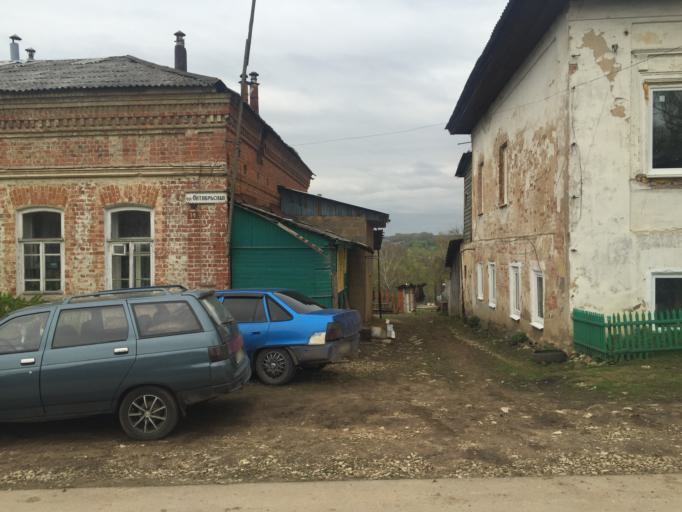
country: RU
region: Tula
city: Krapivna
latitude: 53.9418
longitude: 37.1595
